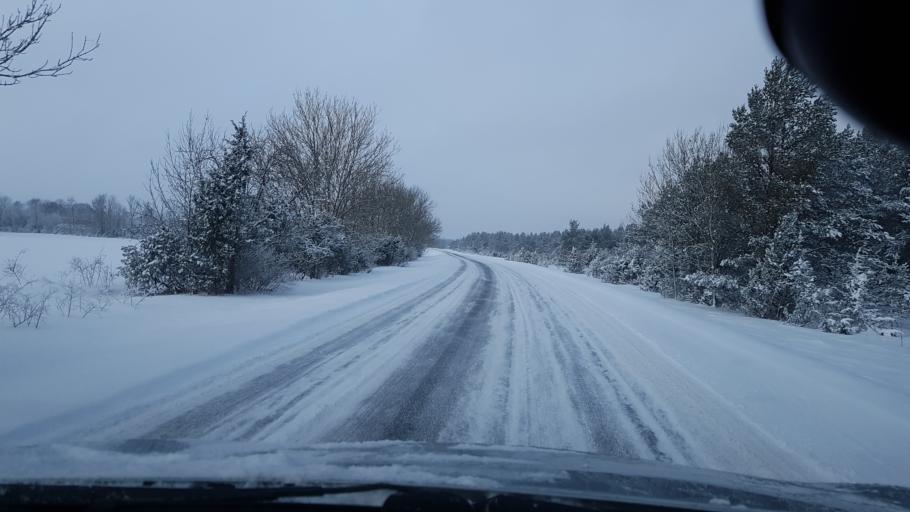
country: EE
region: Harju
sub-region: Keila linn
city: Keila
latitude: 59.3634
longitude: 24.4137
